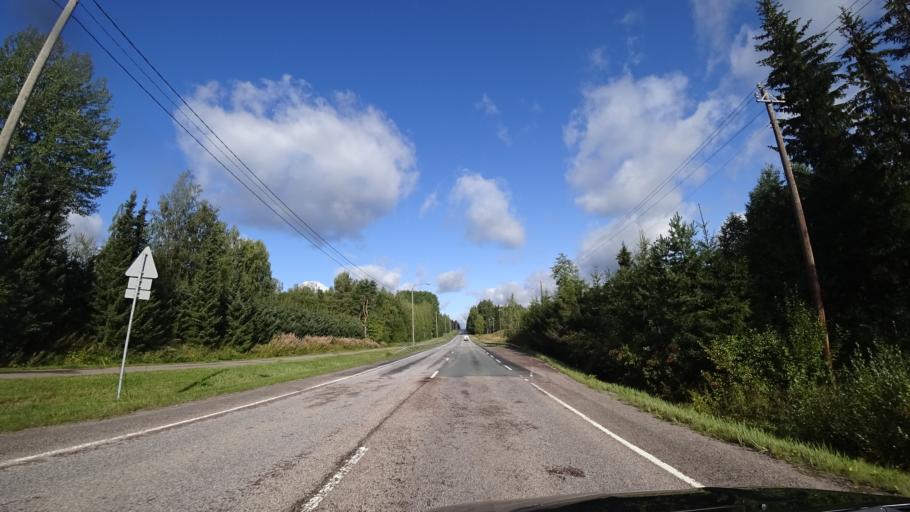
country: FI
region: Uusimaa
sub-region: Helsinki
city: Tuusula
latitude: 60.4345
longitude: 24.9868
